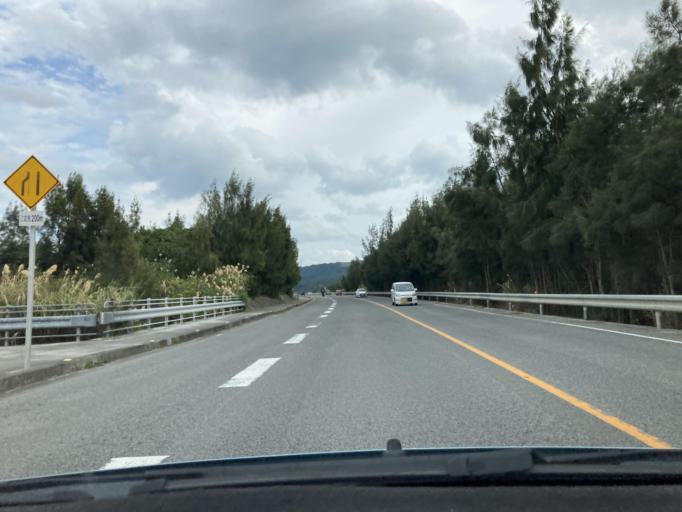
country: JP
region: Okinawa
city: Ishikawa
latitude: 26.4477
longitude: 127.8131
